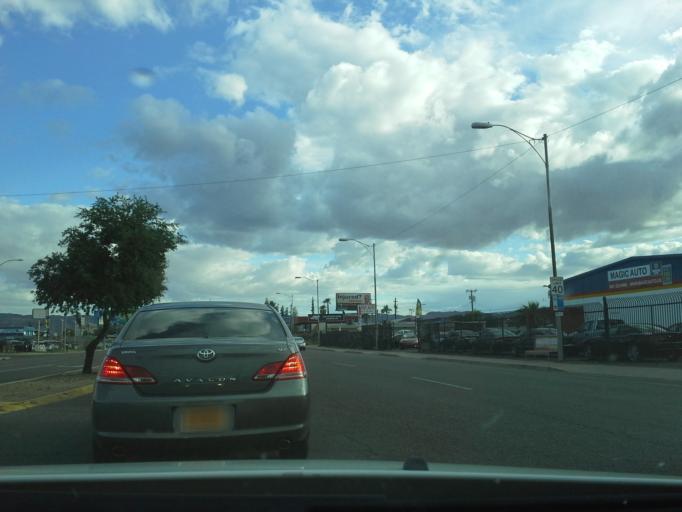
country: US
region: Arizona
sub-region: Maricopa County
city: Phoenix
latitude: 33.4332
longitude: -112.0652
